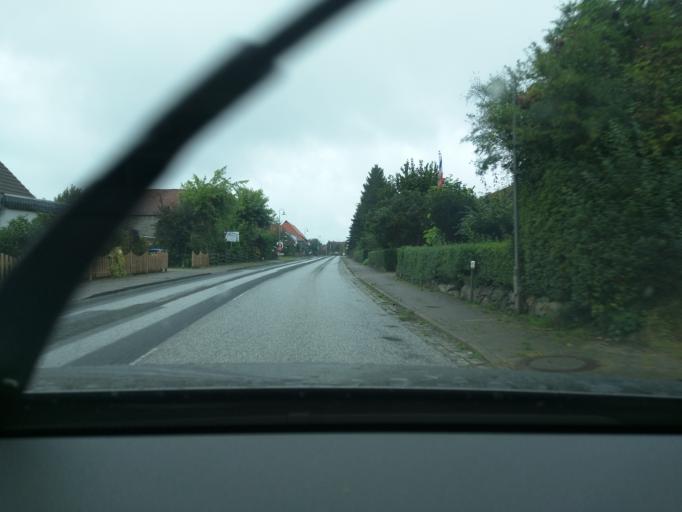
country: DE
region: Schleswig-Holstein
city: Lutau
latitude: 53.4313
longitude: 10.5454
